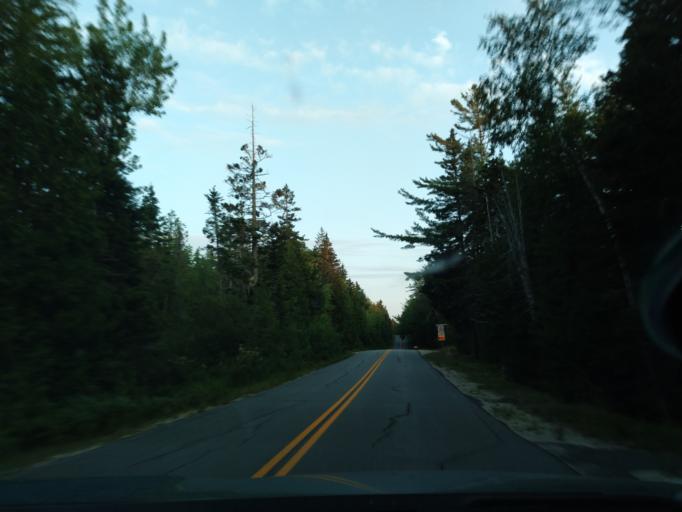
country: US
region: Maine
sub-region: Hancock County
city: Gouldsboro
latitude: 44.3847
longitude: -68.0695
